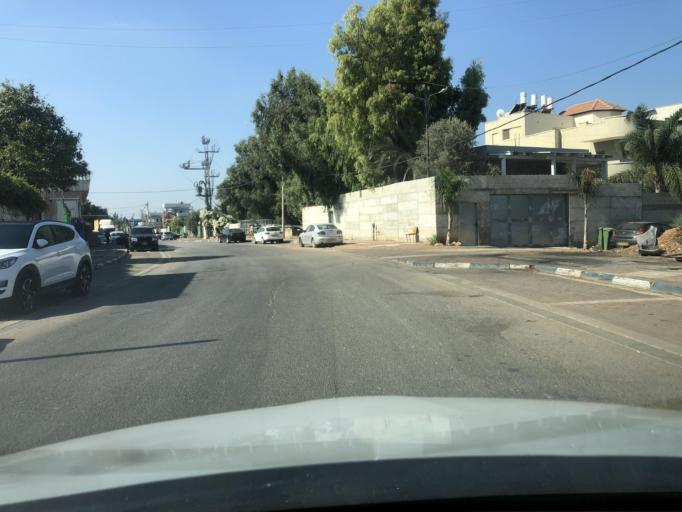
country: IL
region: Central District
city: Jaljulya
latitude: 32.1558
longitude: 34.9493
